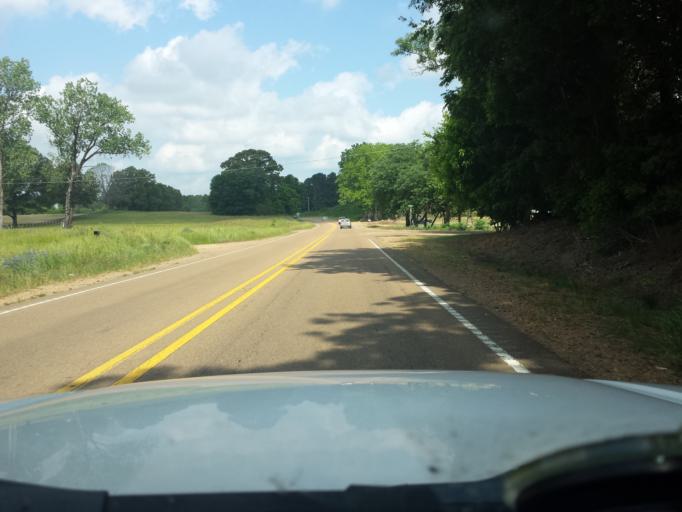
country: US
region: Mississippi
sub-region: Yazoo County
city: Yazoo City
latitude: 32.8311
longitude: -90.2987
